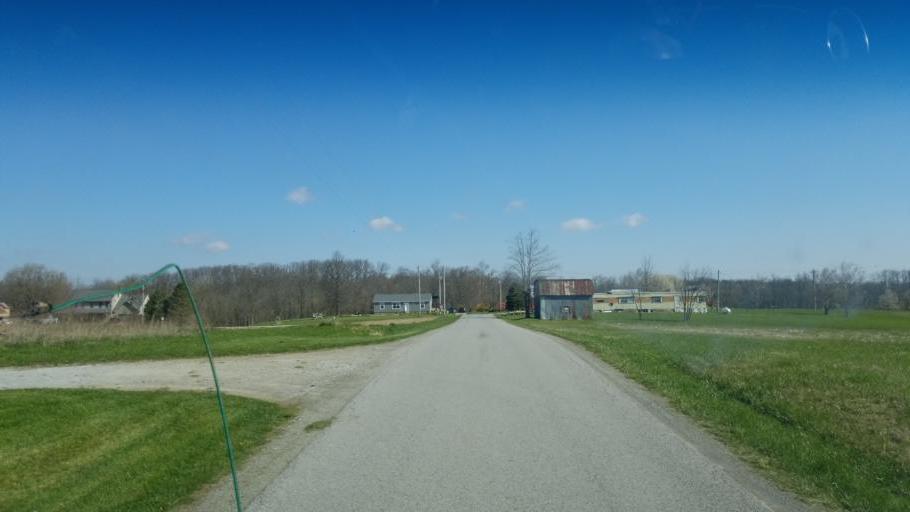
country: US
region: Ohio
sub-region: Hardin County
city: Forest
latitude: 40.7361
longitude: -83.4004
